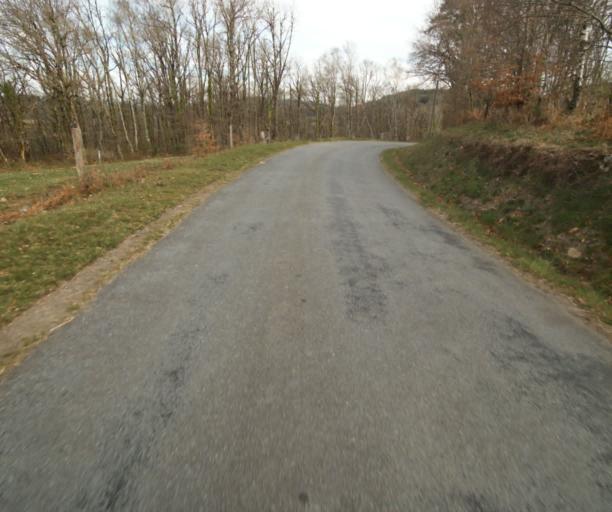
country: FR
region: Limousin
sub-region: Departement de la Correze
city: Treignac
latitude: 45.4681
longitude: 1.8188
